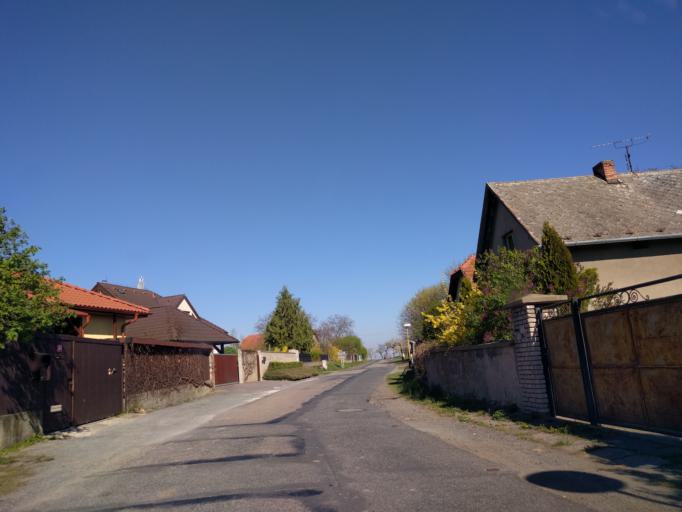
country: CZ
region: Central Bohemia
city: Mukarov
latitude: 49.9875
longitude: 14.7864
